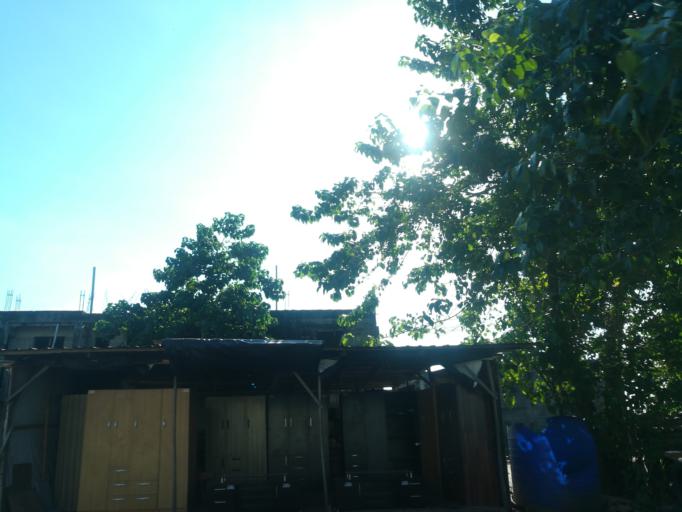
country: NG
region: Lagos
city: Ikorodu
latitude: 6.5644
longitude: 3.5349
